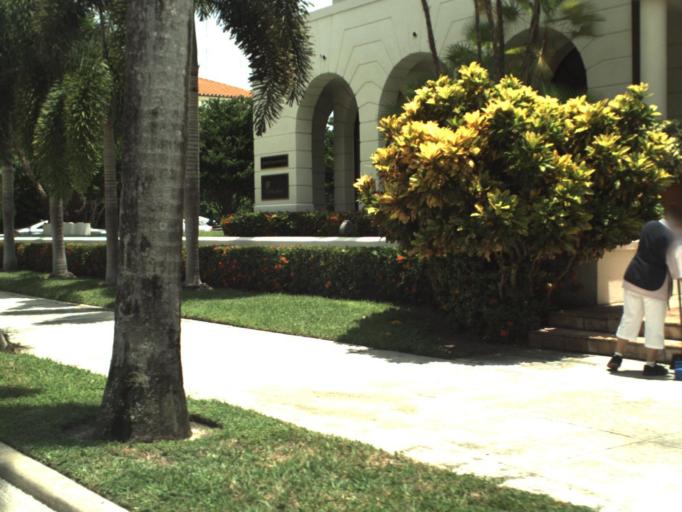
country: US
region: Florida
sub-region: Palm Beach County
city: Palm Beach
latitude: 26.7057
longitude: -80.0426
